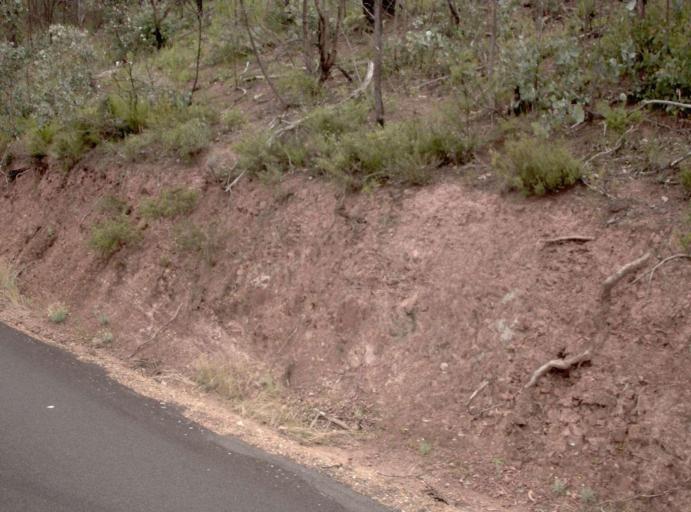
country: AU
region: Victoria
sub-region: Wellington
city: Heyfield
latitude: -37.7133
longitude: 146.6687
